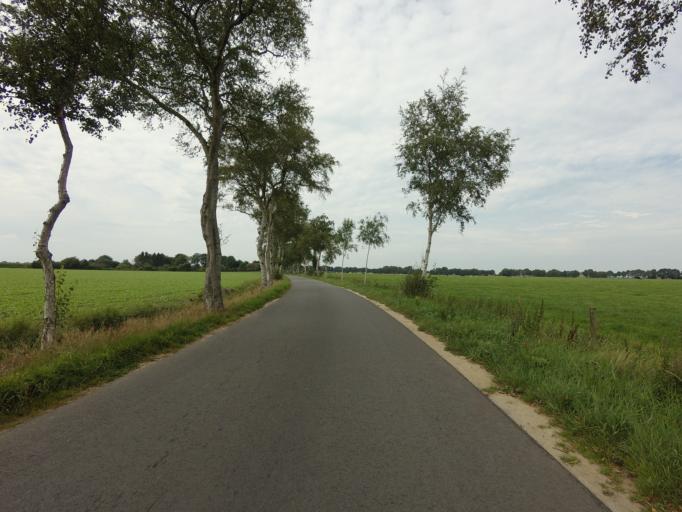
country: NL
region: Drenthe
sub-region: Gemeente Westerveld
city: Dwingeloo
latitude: 52.8274
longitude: 6.3875
